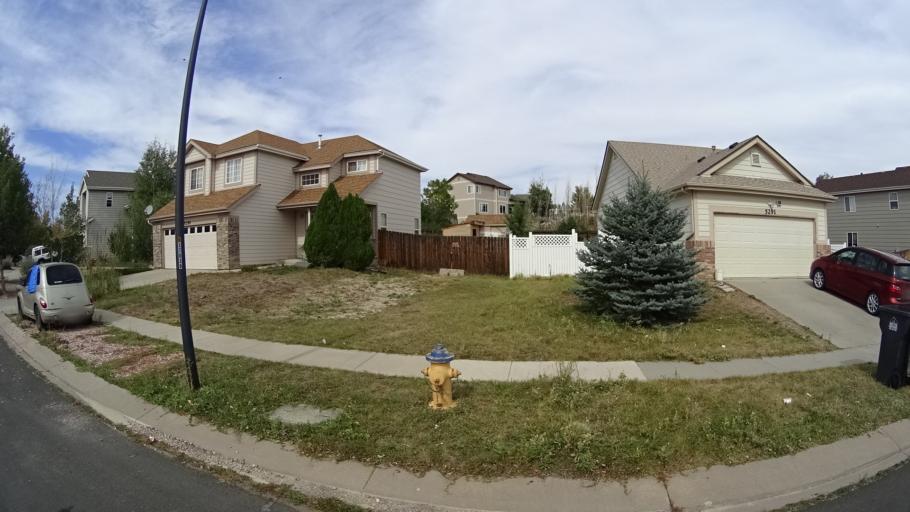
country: US
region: Colorado
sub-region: El Paso County
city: Cimarron Hills
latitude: 38.9088
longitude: -104.6984
